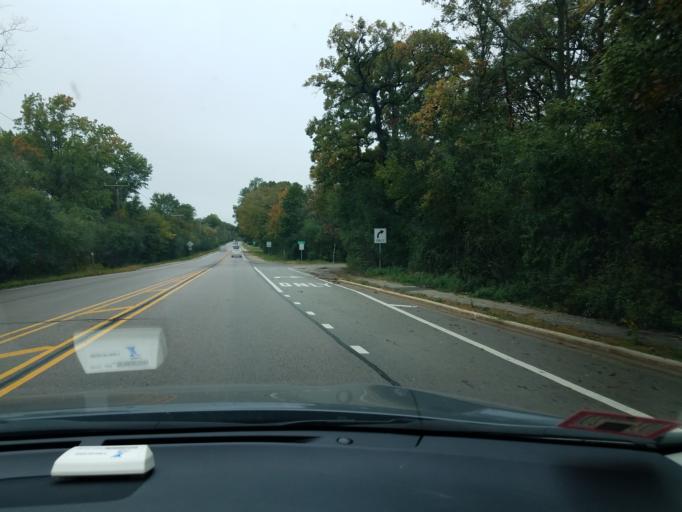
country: US
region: Illinois
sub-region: Lake County
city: Riverwoods
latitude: 42.1675
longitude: -87.8853
